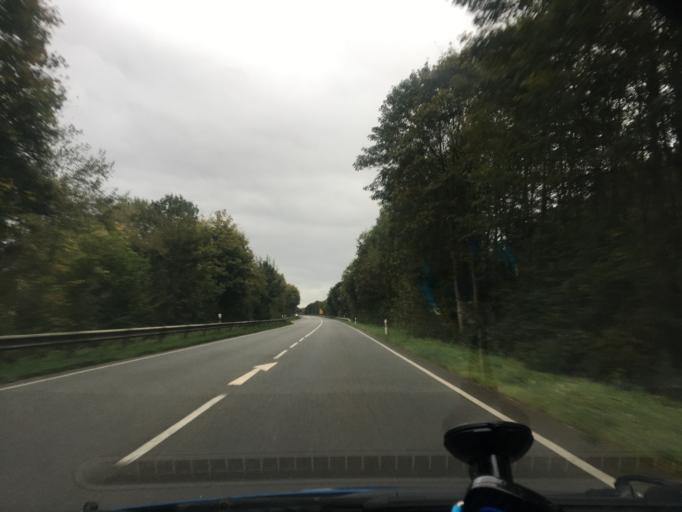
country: DE
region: Lower Saxony
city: Handorf
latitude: 53.3423
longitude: 10.3352
